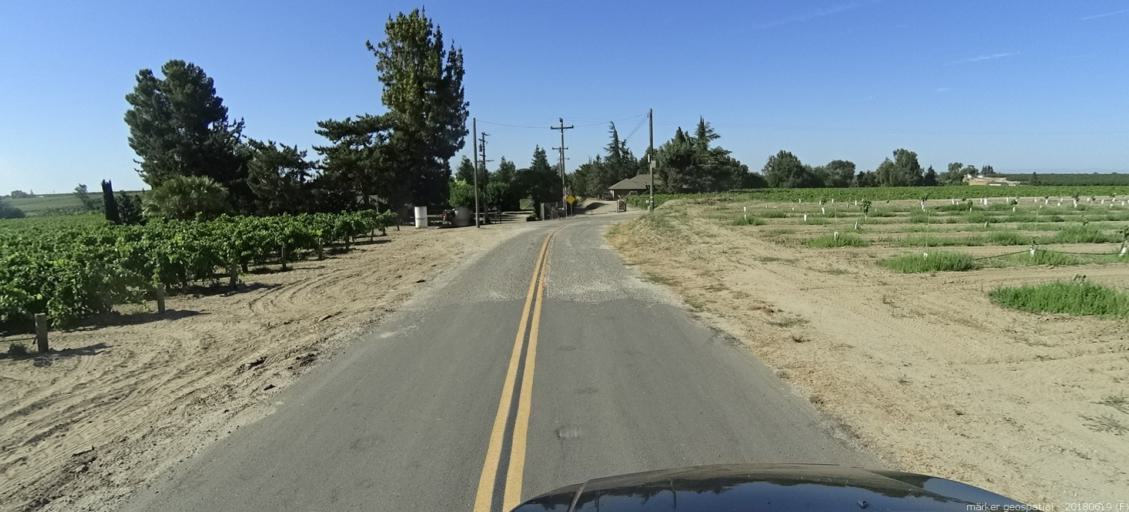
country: US
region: California
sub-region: Fresno County
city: Biola
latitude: 36.8300
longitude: -120.0156
